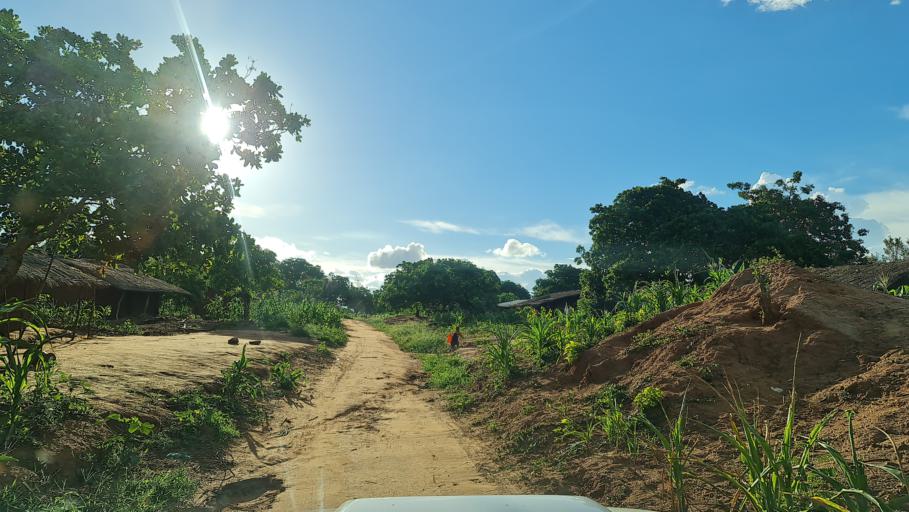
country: MZ
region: Nampula
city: Ilha de Mocambique
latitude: -14.9442
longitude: 40.1630
